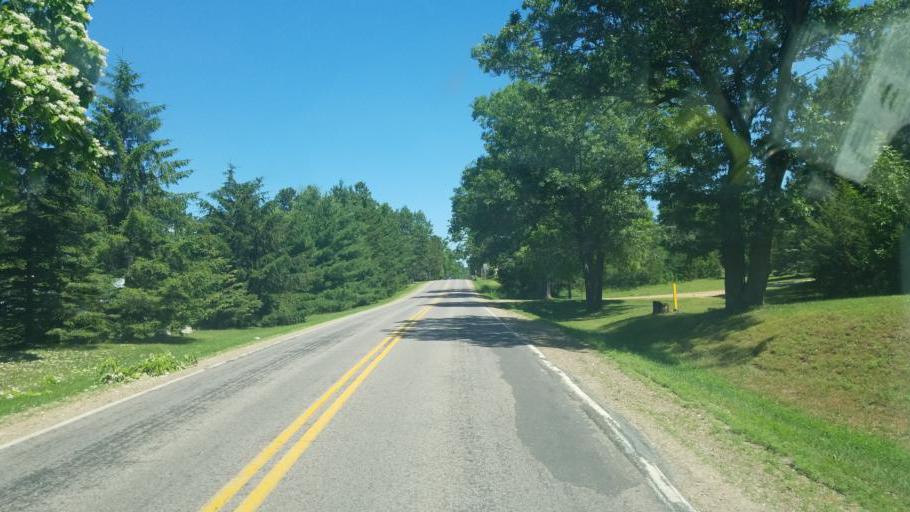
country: US
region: Wisconsin
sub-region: Adams County
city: Adams
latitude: 43.9092
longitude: -89.9378
